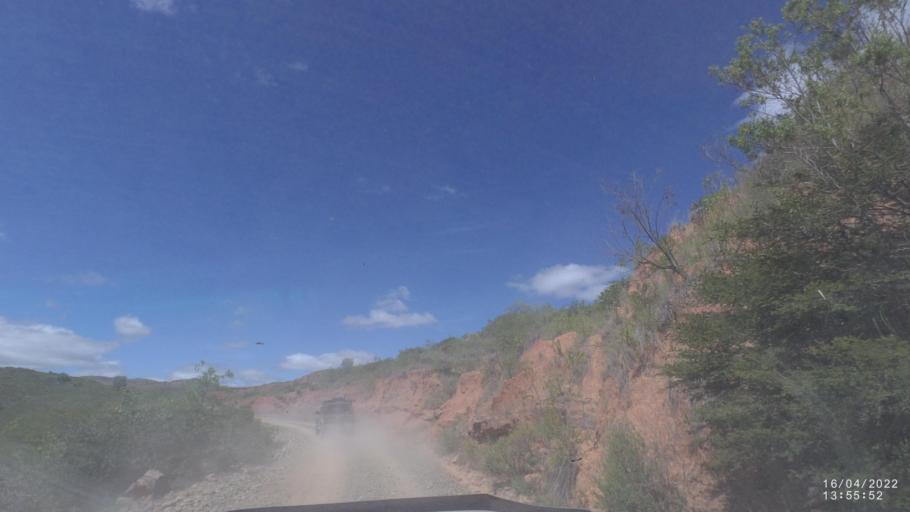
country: BO
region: Cochabamba
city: Mizque
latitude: -18.0307
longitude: -65.5649
